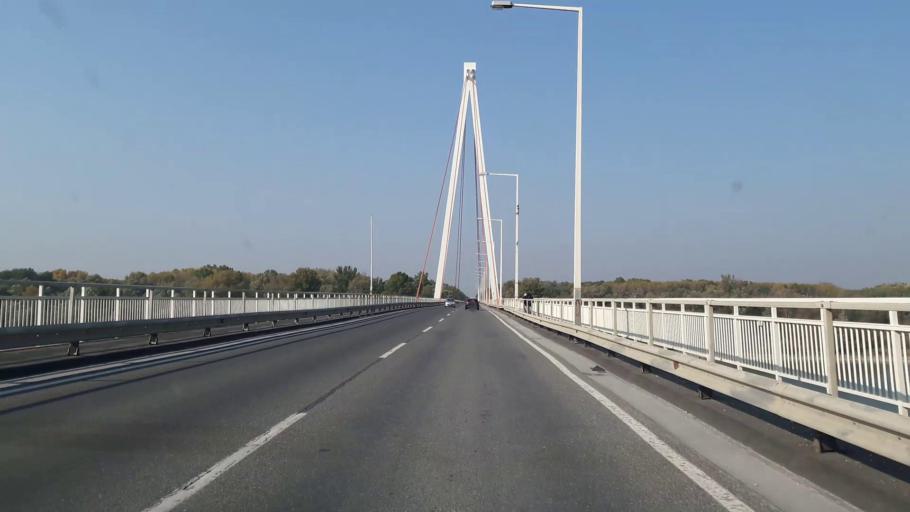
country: AT
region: Lower Austria
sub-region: Politischer Bezirk Bruck an der Leitha
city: Bad Deutsch-Altenburg
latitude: 48.1445
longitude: 16.9093
